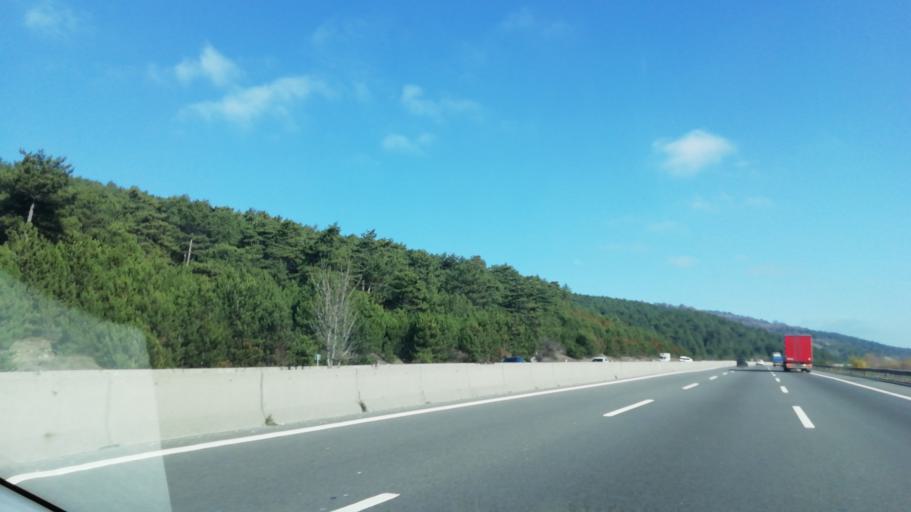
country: TR
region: Bolu
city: Gokcesu
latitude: 40.7375
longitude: 31.8196
